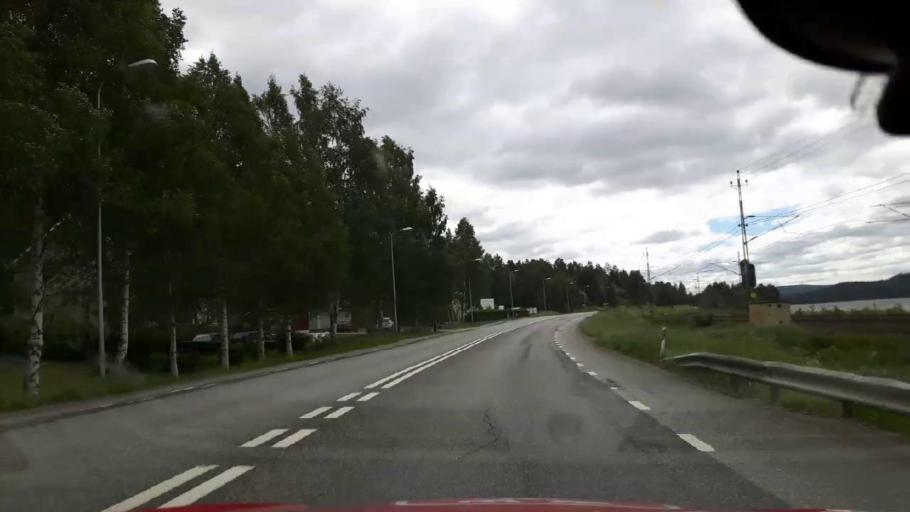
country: SE
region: Jaemtland
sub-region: Braecke Kommun
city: Braecke
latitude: 62.7440
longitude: 15.4256
